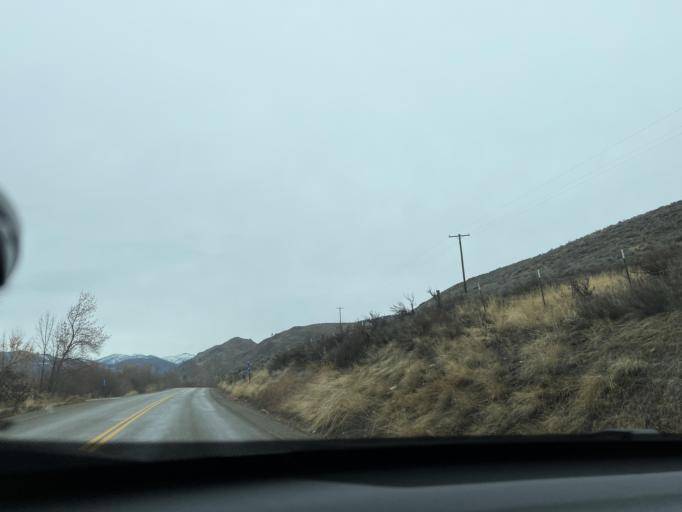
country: US
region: Washington
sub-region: Okanogan County
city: Brewster
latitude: 48.5051
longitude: -120.1738
